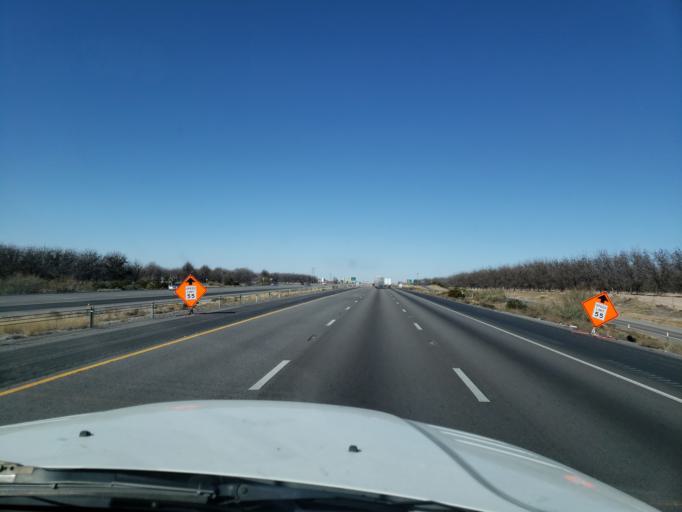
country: US
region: New Mexico
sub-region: Dona Ana County
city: University Park
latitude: 32.2377
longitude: -106.7155
